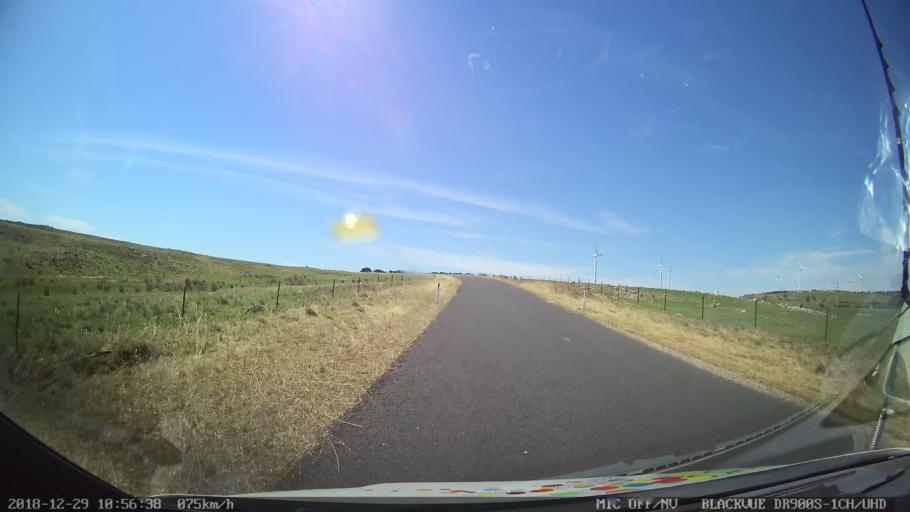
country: AU
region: New South Wales
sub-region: Palerang
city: Bungendore
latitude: -35.1363
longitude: 149.5394
